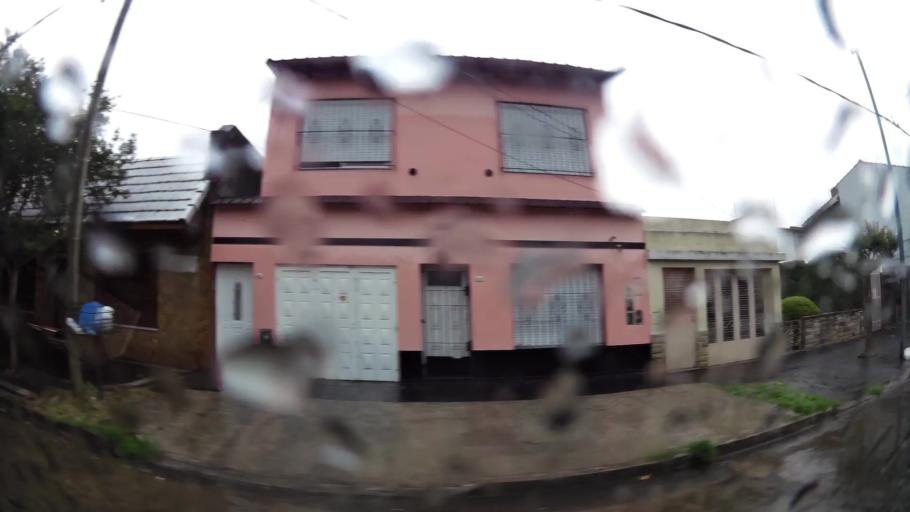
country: AR
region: Buenos Aires
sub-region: Partido de Lanus
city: Lanus
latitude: -34.7083
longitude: -58.4077
